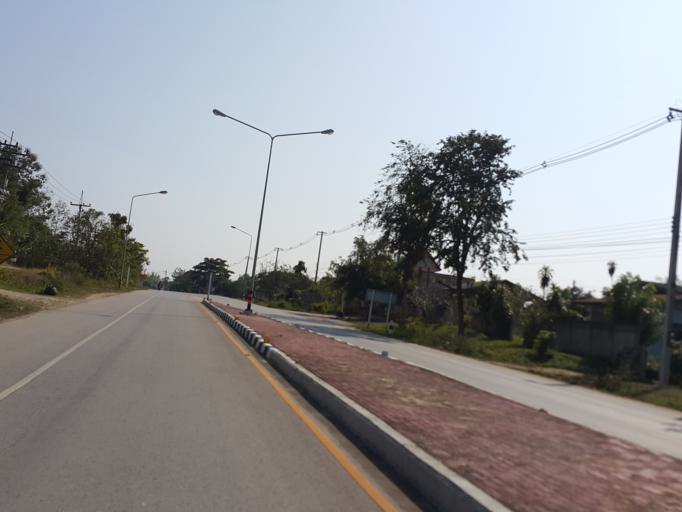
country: TH
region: Lampang
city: Chae Hom
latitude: 18.7550
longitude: 99.5714
